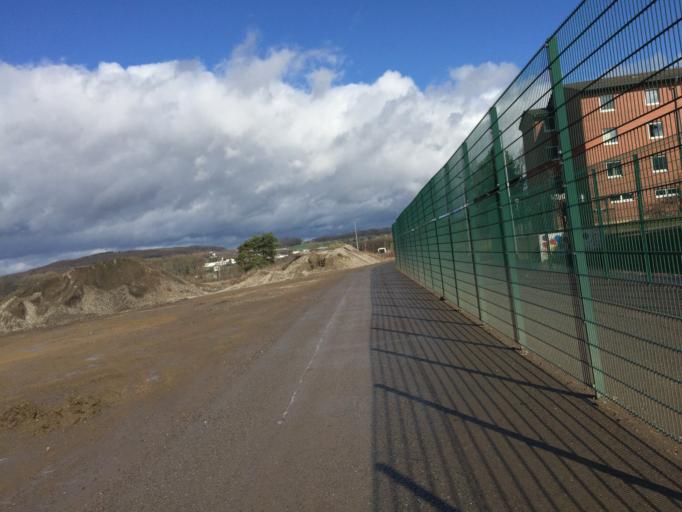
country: DE
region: Hesse
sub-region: Regierungsbezirk Giessen
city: Alten Buseck
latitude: 50.5964
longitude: 8.7322
